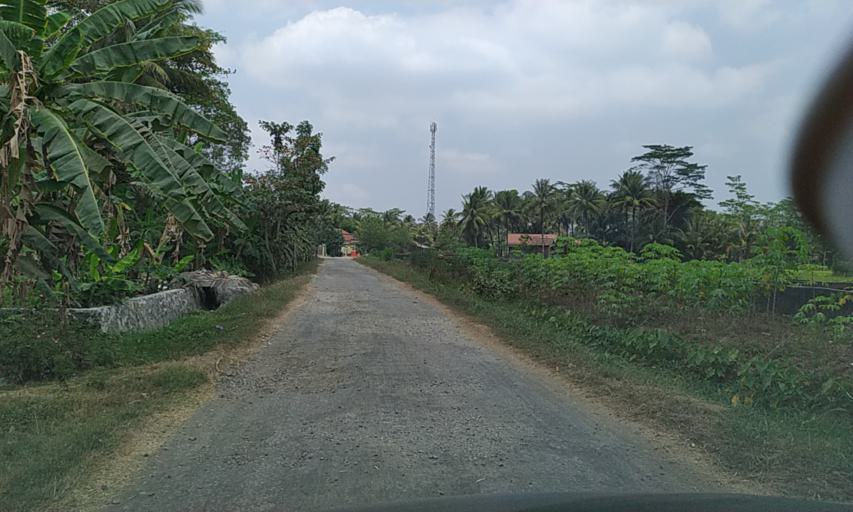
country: ID
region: Central Java
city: Sidakaya
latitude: -7.5765
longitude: 108.8631
